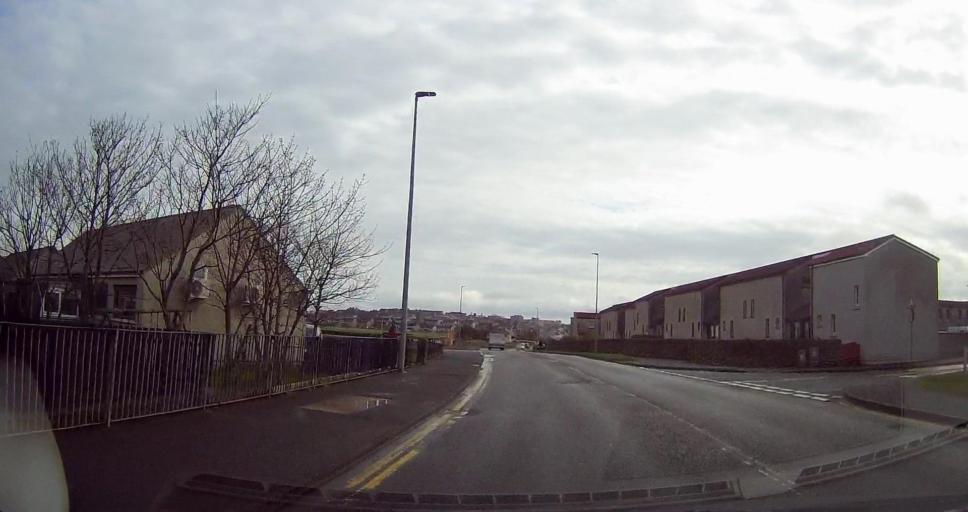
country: GB
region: Scotland
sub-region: Shetland Islands
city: Lerwick
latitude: 60.1463
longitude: -1.1686
